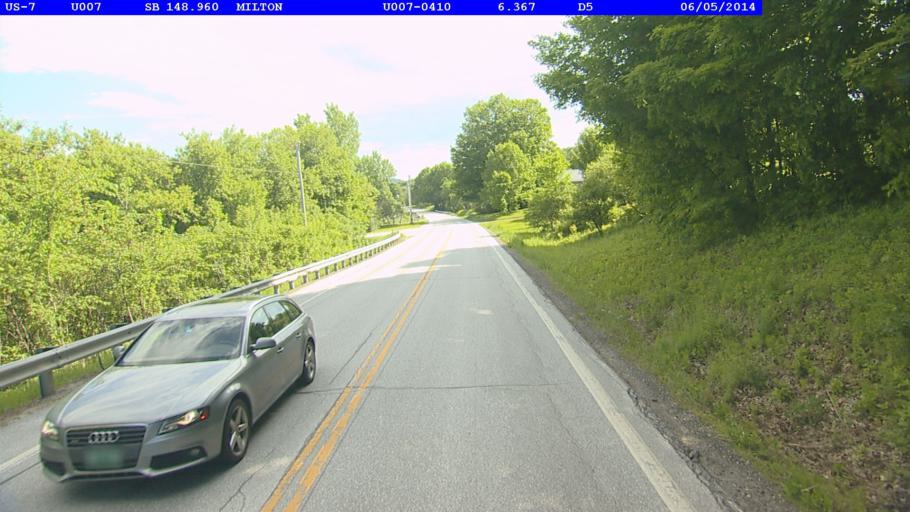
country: US
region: Vermont
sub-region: Chittenden County
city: Milton
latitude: 44.6582
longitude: -73.1126
